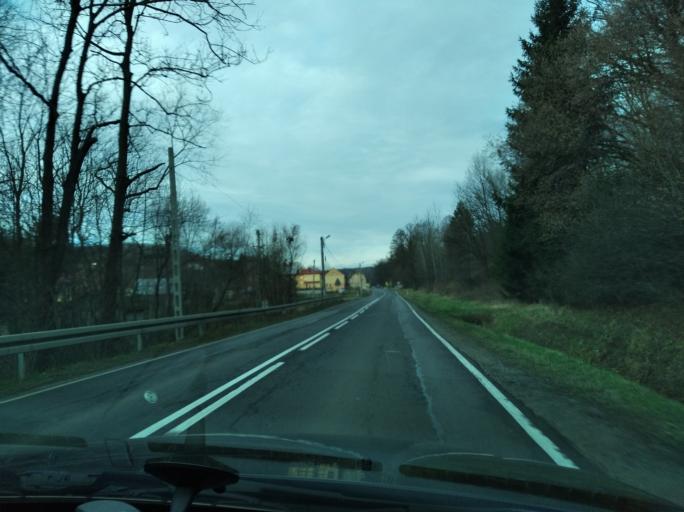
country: PL
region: Subcarpathian Voivodeship
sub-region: Powiat strzyzowski
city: Wisniowa
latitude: 49.9014
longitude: 21.6341
